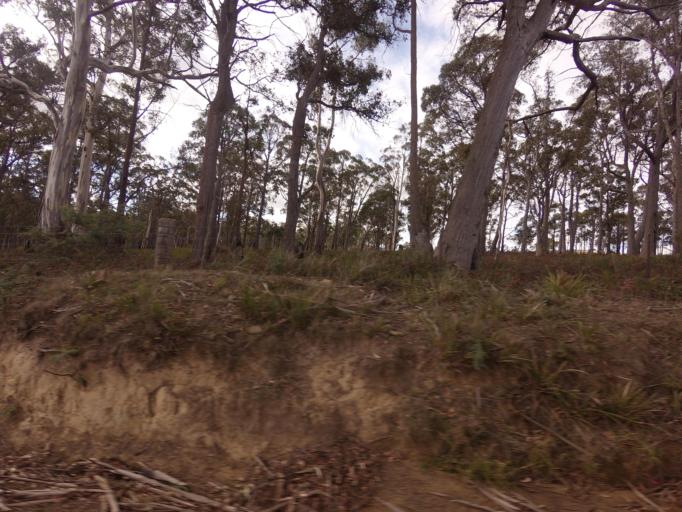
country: AU
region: Tasmania
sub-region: Brighton
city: Bridgewater
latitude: -42.4912
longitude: 147.3151
